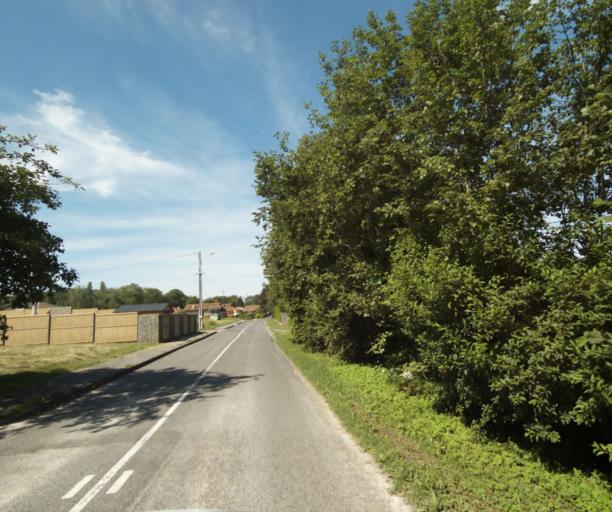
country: FR
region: Rhone-Alpes
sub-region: Departement de la Haute-Savoie
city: Anthy-sur-Leman
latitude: 46.3584
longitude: 6.4411
